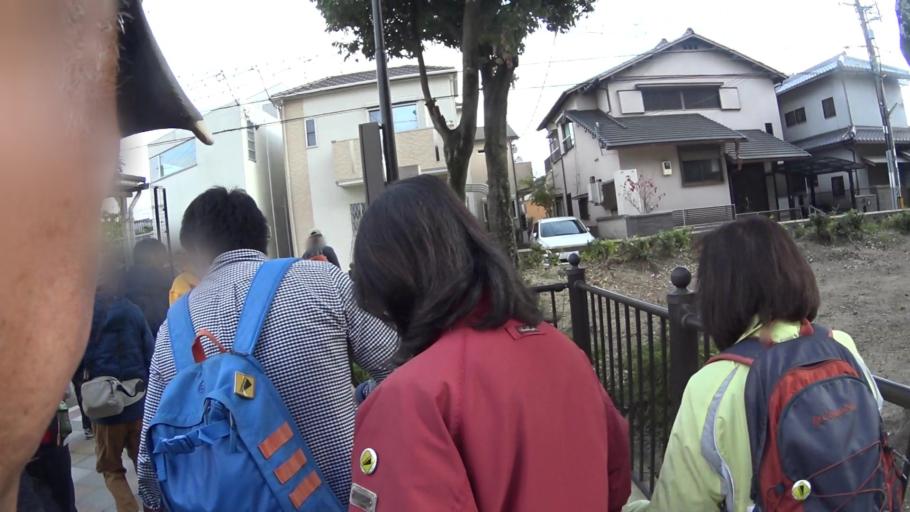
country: JP
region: Kyoto
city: Yawata
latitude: 34.8812
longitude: 135.6641
